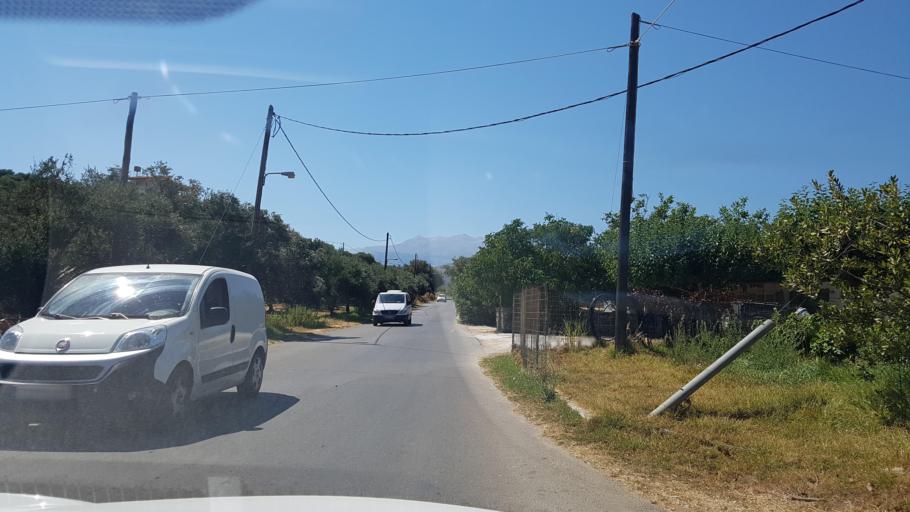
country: GR
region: Crete
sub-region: Nomos Chanias
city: Daratsos
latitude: 35.5033
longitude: 23.9897
